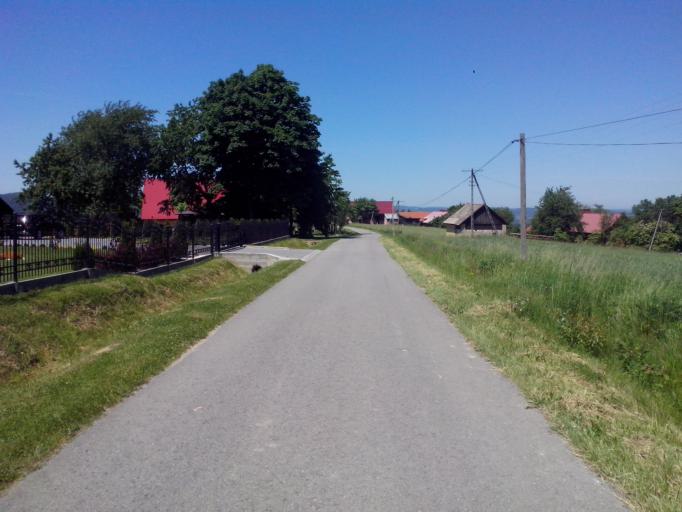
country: PL
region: Subcarpathian Voivodeship
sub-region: Powiat strzyzowski
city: Wysoka Strzyzowska
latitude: 49.8161
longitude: 21.7738
